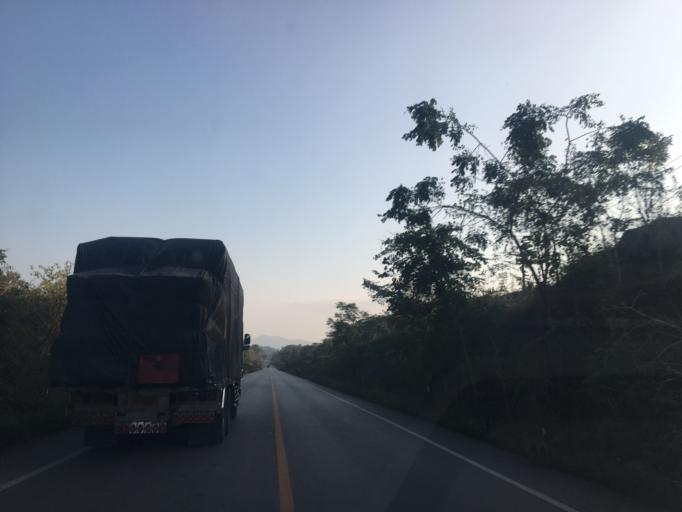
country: TH
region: Lampang
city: Ngao
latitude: 18.6500
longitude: 100.0178
